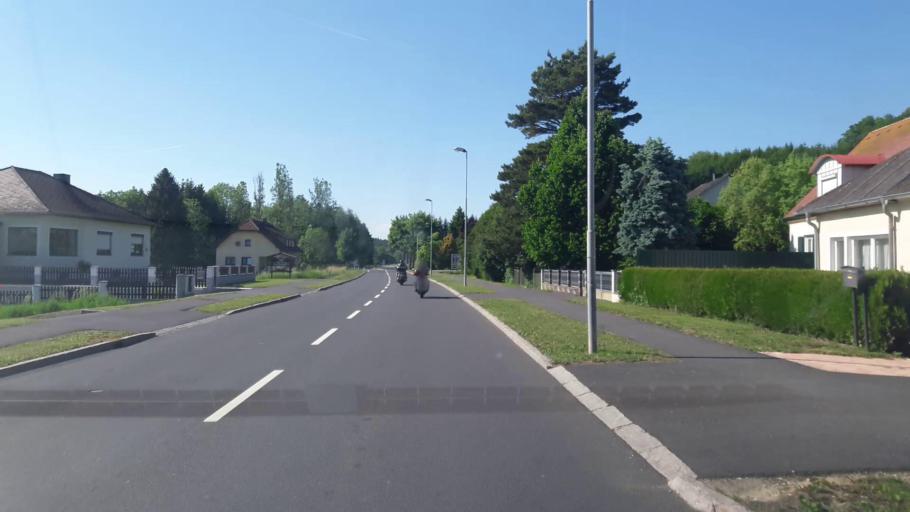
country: AT
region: Burgenland
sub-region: Politischer Bezirk Gussing
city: Ollersdorf im Burgenland
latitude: 47.1892
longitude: 16.1637
